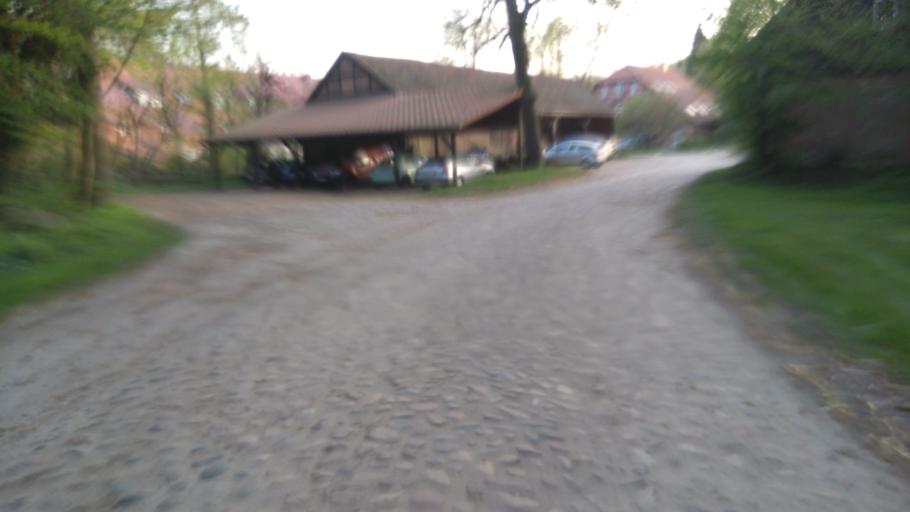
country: DE
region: Lower Saxony
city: Bliedersdorf
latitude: 53.4986
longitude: 9.5564
